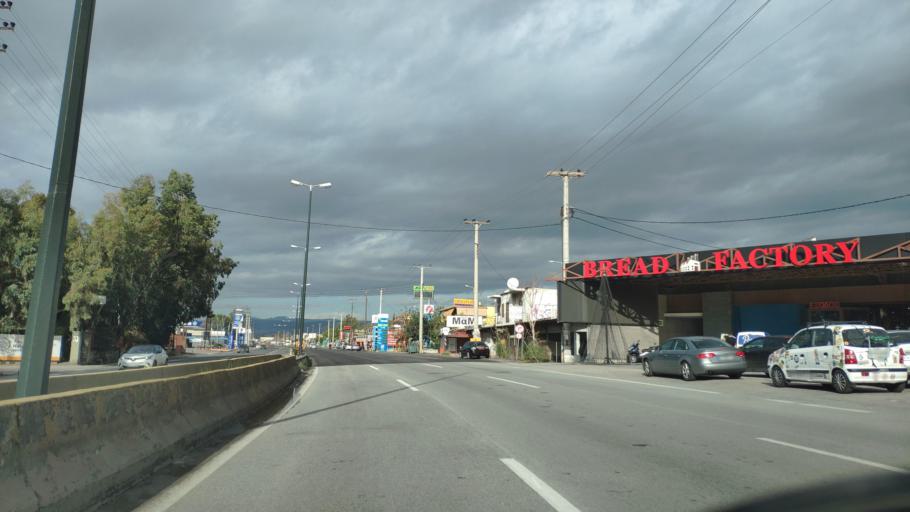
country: GR
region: Attica
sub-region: Nomarchia Dytikis Attikis
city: Aspropyrgos
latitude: 38.0370
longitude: 23.5930
